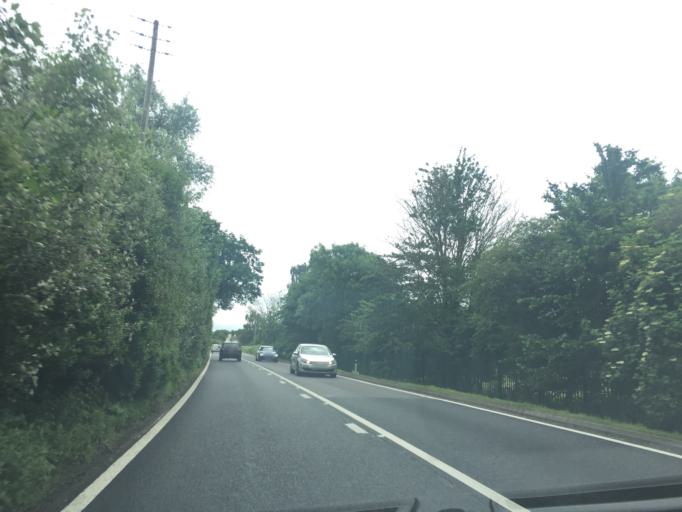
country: GB
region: England
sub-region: Dorset
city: Lytchett Matravers
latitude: 50.7861
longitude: -2.0420
